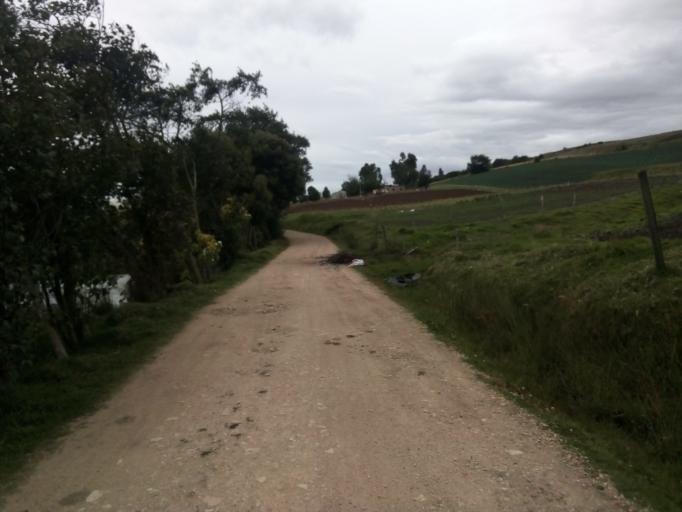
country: CO
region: Boyaca
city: Toca
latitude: 5.5848
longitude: -73.1418
